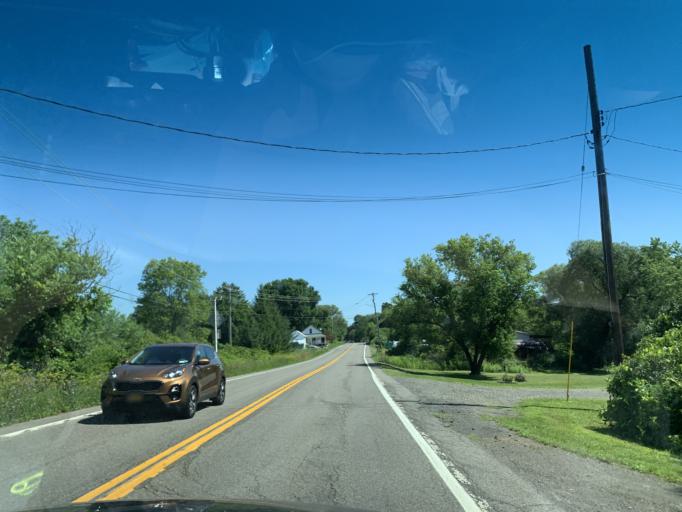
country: US
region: New York
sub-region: Chenango County
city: Norwich
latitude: 42.5094
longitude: -75.4046
